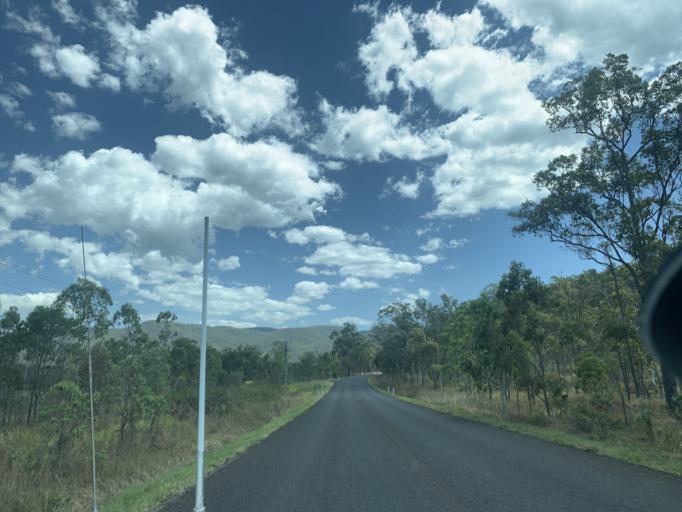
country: AU
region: Queensland
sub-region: Tablelands
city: Atherton
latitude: -17.3088
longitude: 145.4568
